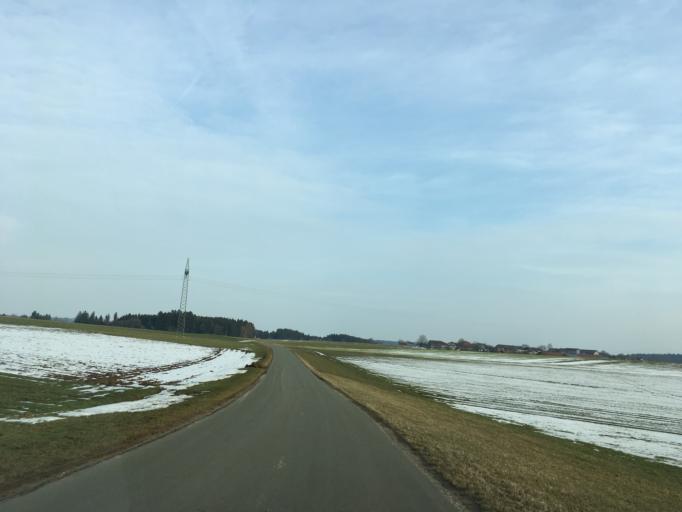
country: DE
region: Bavaria
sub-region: Upper Bavaria
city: Sochtenau
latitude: 47.9452
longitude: 12.2242
